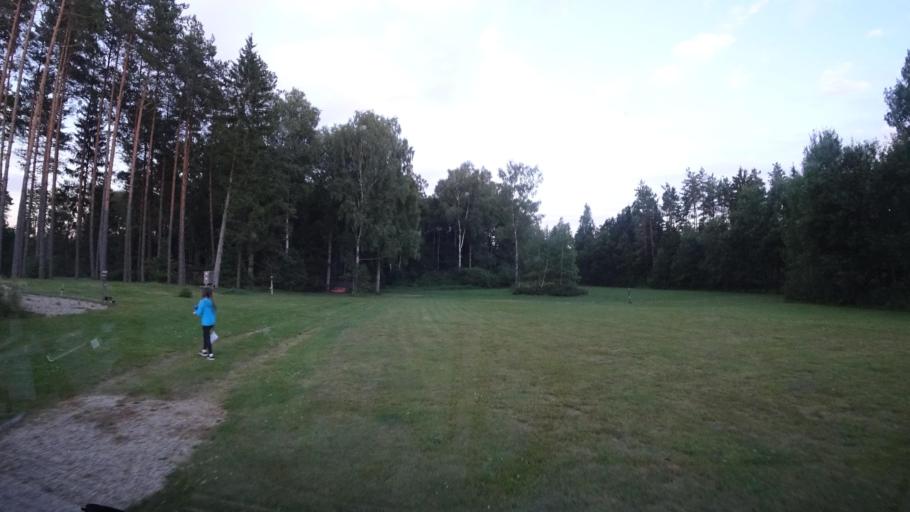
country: LT
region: Vilnius County
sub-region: Trakai
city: Rudiskes
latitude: 54.5072
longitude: 24.8904
